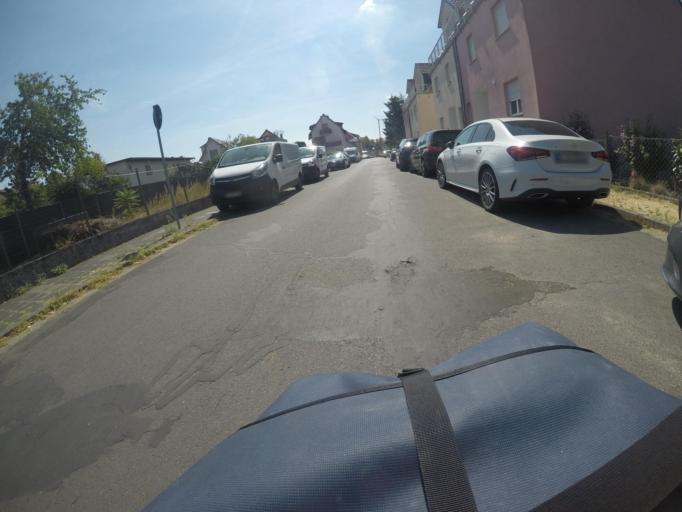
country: DE
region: Hesse
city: Kelsterbach
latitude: 50.0742
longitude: 8.5288
